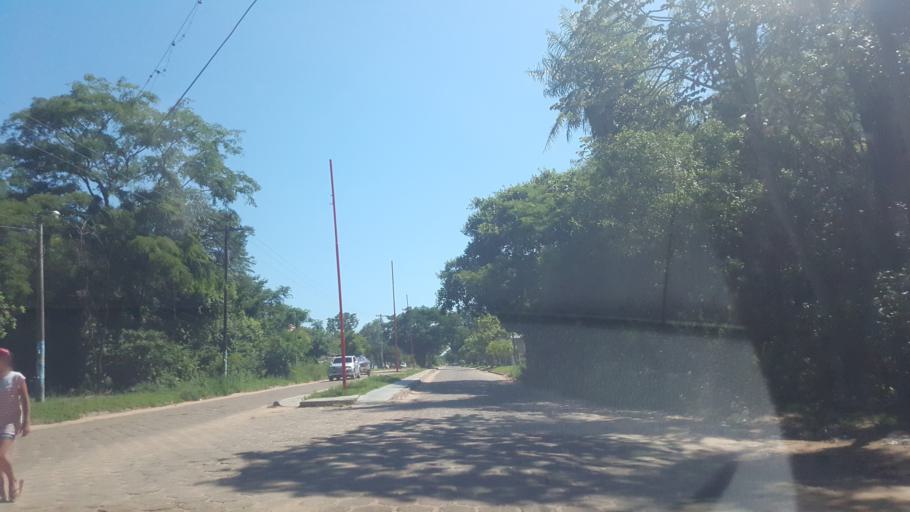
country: AR
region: Corrientes
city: Ituzaingo
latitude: -27.5924
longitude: -56.7018
